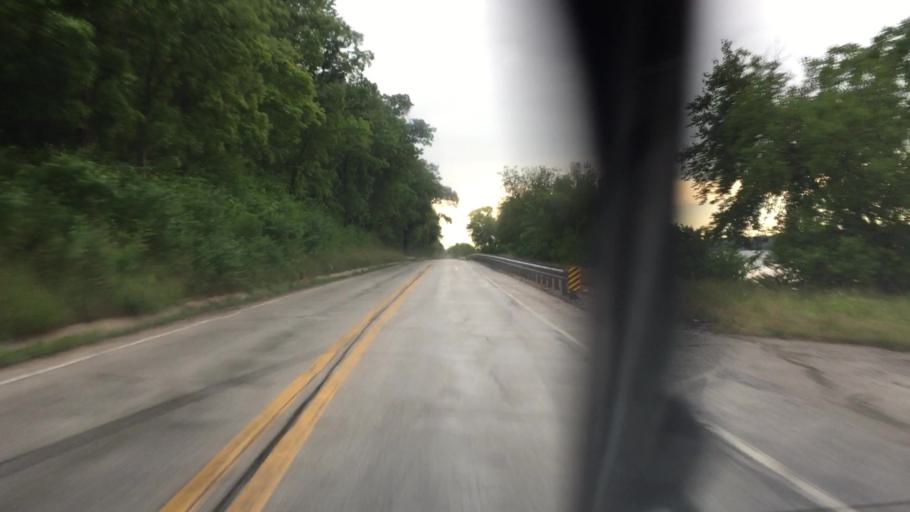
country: US
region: Iowa
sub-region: Lee County
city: Keokuk
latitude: 40.4641
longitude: -91.3630
